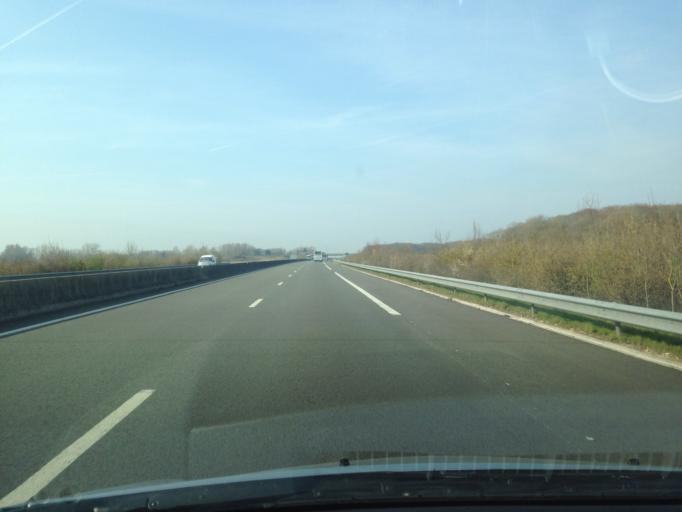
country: FR
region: Nord-Pas-de-Calais
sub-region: Departement du Pas-de-Calais
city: Verton
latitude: 50.3923
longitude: 1.6951
